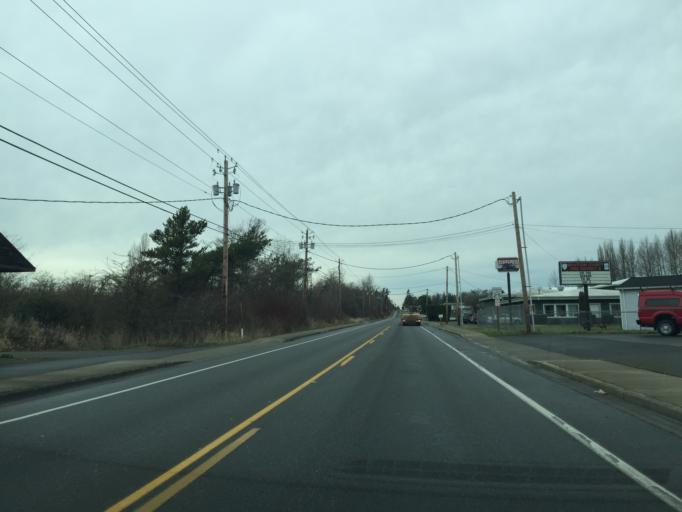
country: US
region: Washington
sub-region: Whatcom County
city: Bellingham
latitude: 48.7689
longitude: -122.5205
